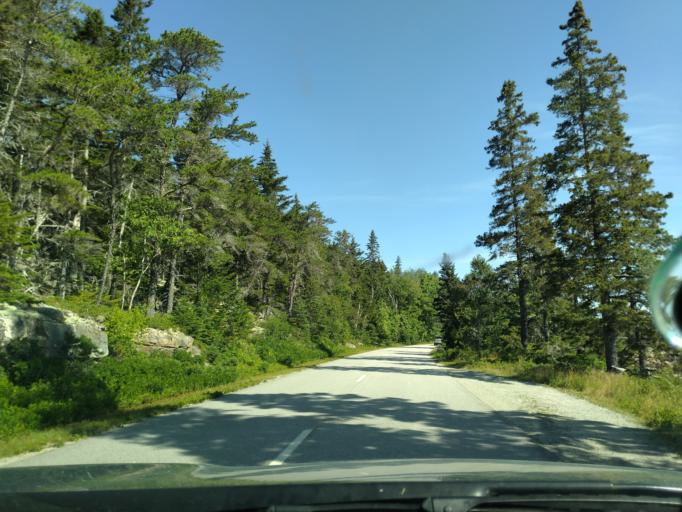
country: US
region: Maine
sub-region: Hancock County
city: Gouldsboro
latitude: 44.3572
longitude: -68.0468
